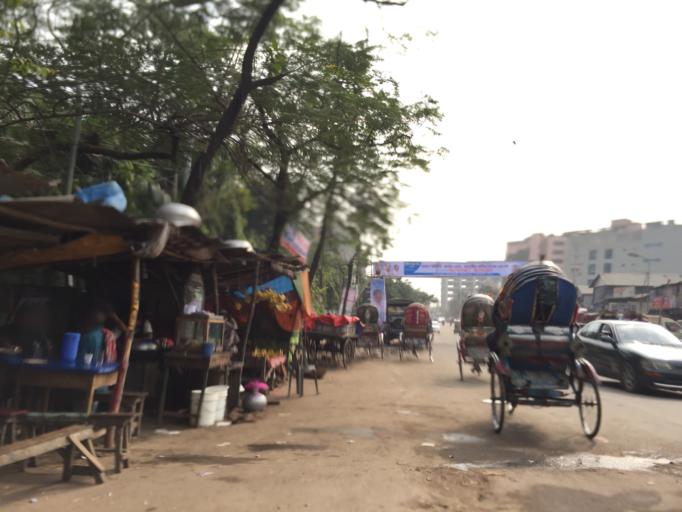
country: BD
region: Dhaka
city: Azimpur
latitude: 23.7787
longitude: 90.3709
